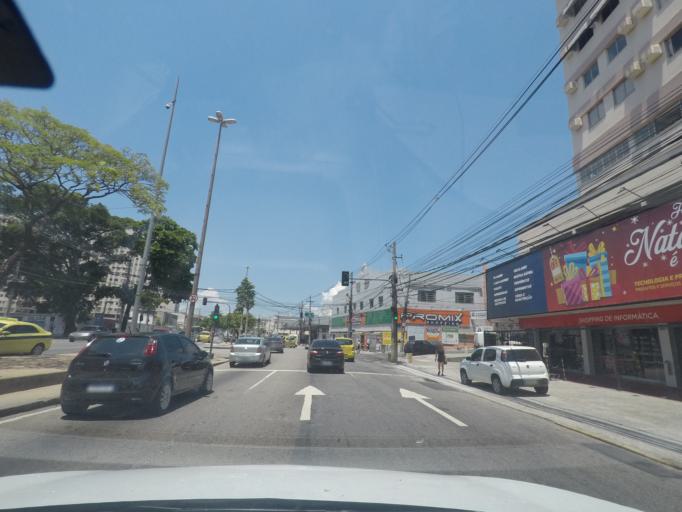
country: BR
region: Rio de Janeiro
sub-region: Rio De Janeiro
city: Rio de Janeiro
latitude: -22.8870
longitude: -43.2806
